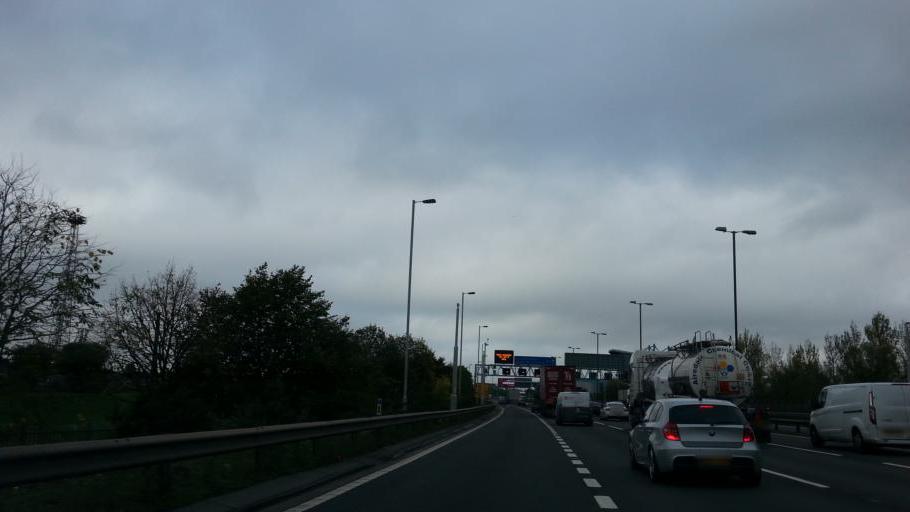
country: GB
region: England
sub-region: Walsall
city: Walsall
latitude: 52.5605
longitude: -1.9826
